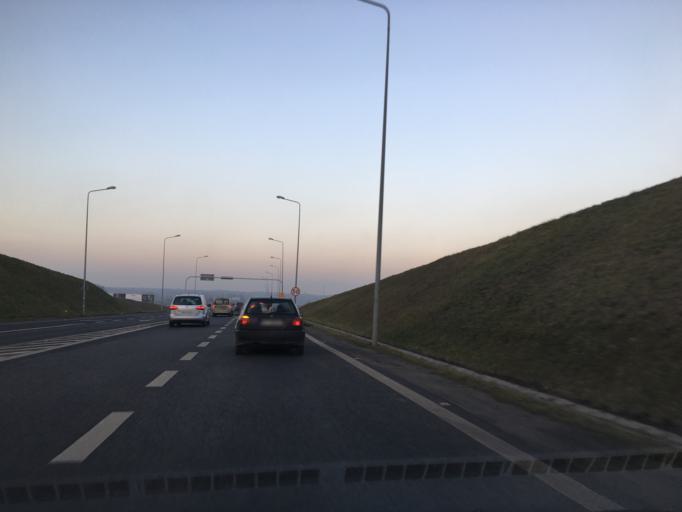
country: PL
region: Silesian Voivodeship
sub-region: Powiat tarnogorski
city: Radzionkow
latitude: 50.3568
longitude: 18.8680
